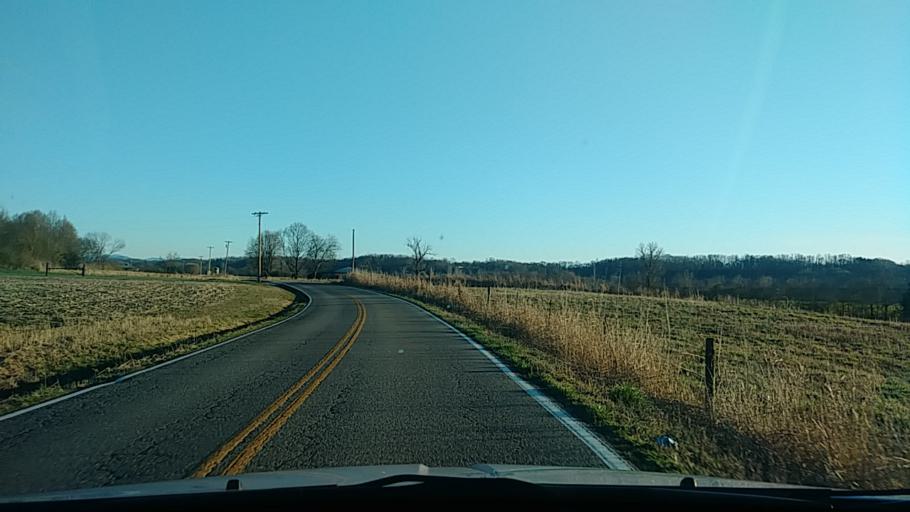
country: US
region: Tennessee
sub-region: Jefferson County
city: White Pine
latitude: 36.1584
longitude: -83.1621
